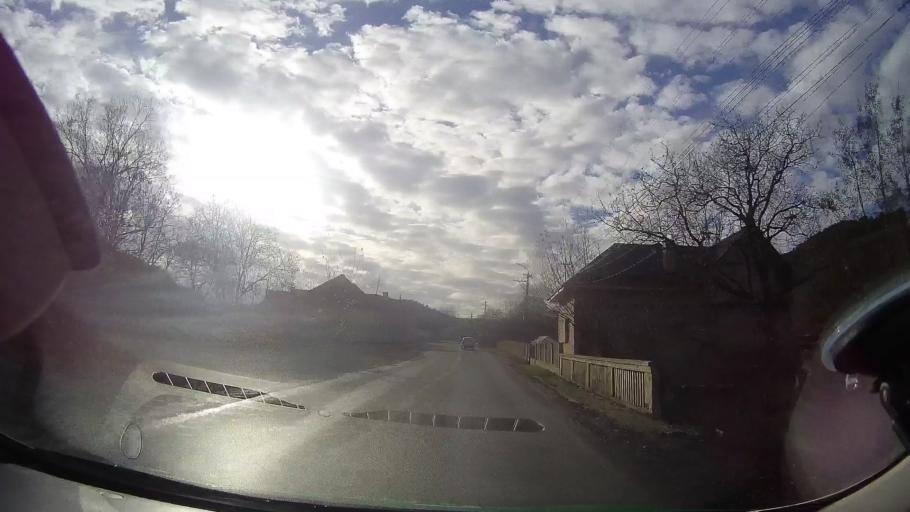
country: RO
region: Cluj
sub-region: Comuna Savadisla
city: Savadisla
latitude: 46.6784
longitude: 23.4566
